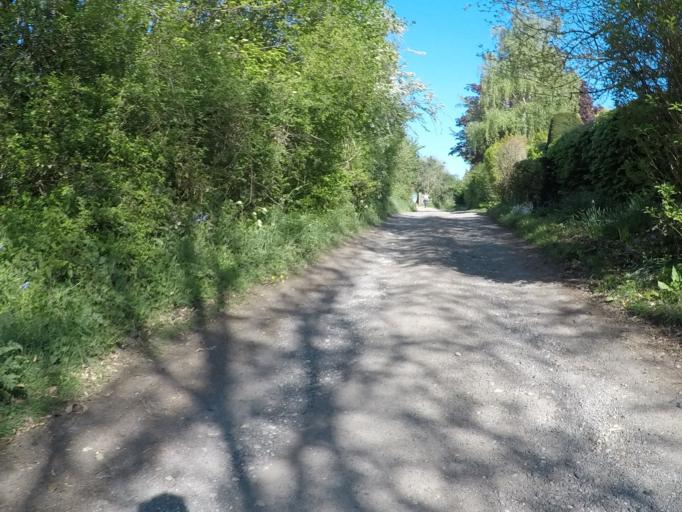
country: GB
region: England
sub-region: Oxfordshire
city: Charlbury
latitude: 51.8658
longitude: -1.4739
